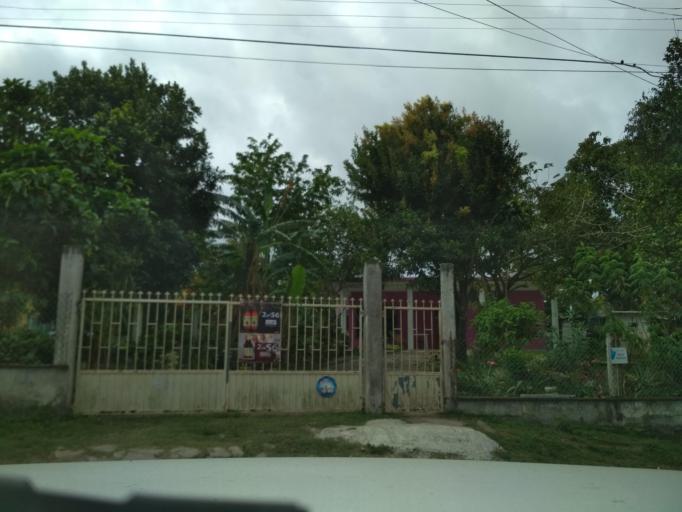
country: MX
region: Veracruz
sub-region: Veracruz
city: Delfino Victoria (Santa Fe)
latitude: 19.2561
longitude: -96.2669
